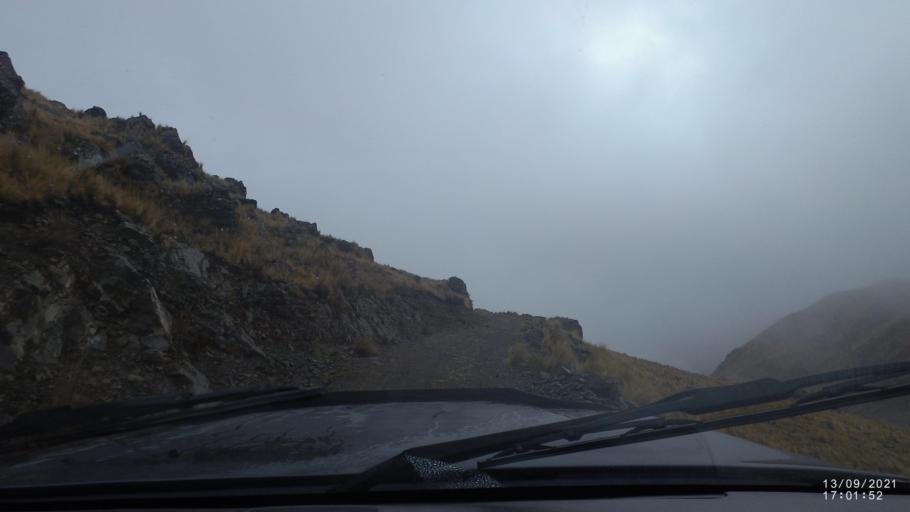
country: BO
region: Cochabamba
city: Colomi
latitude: -17.3152
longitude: -65.7213
